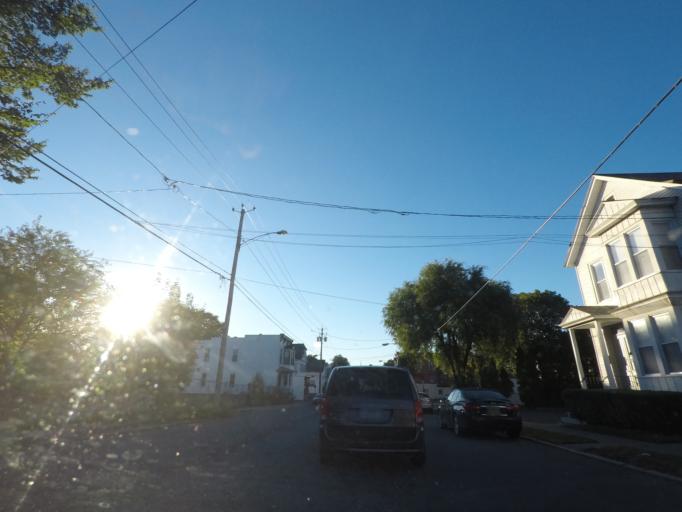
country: US
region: New York
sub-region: Albany County
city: Cohoes
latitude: 42.7728
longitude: -73.6870
